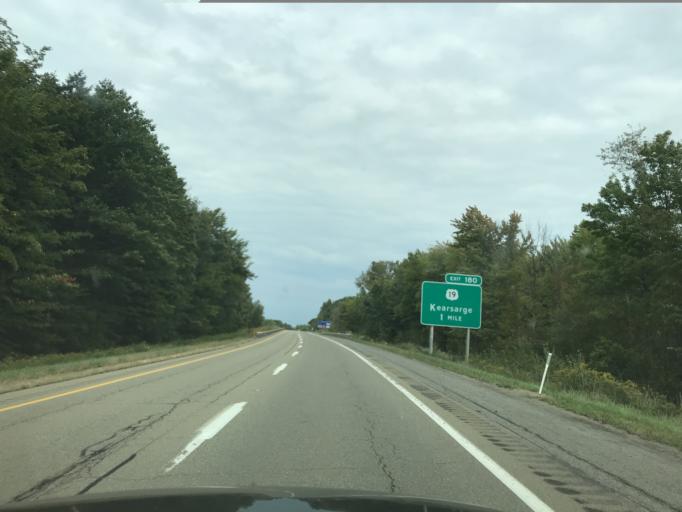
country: US
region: Pennsylvania
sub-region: Erie County
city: Erie
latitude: 42.0503
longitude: -80.1129
